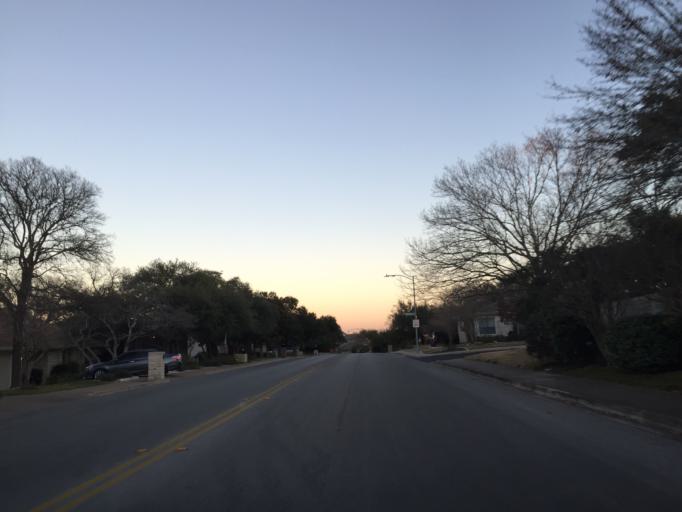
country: US
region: Texas
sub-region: Williamson County
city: Jollyville
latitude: 30.4099
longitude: -97.7658
